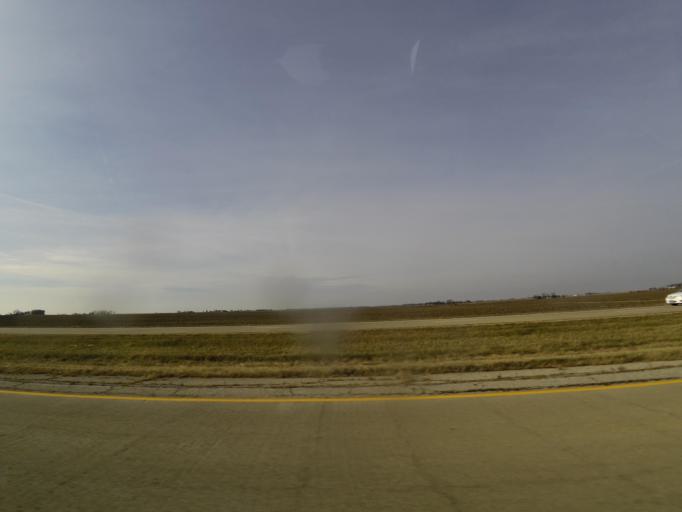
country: US
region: Illinois
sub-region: McLean County
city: Heyworth
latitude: 40.3803
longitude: -88.9895
